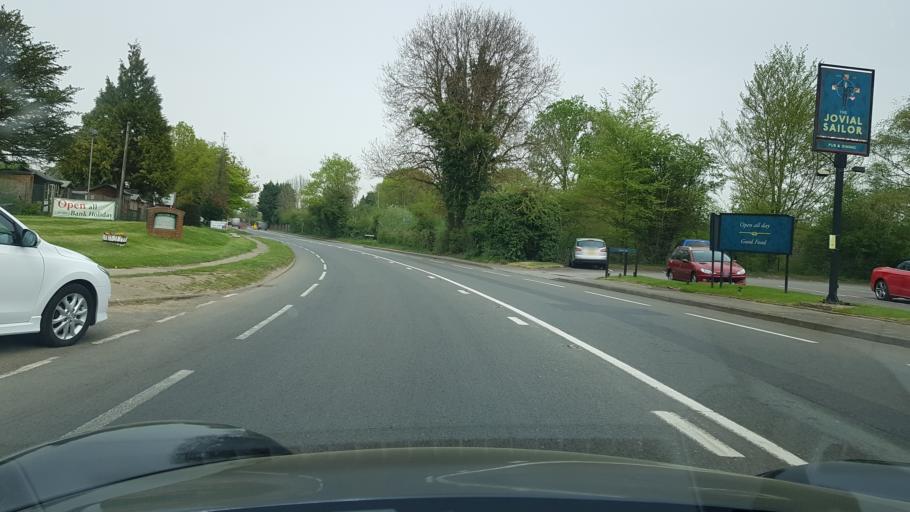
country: GB
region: England
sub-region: Surrey
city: Ripley
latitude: 51.2894
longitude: -0.5022
